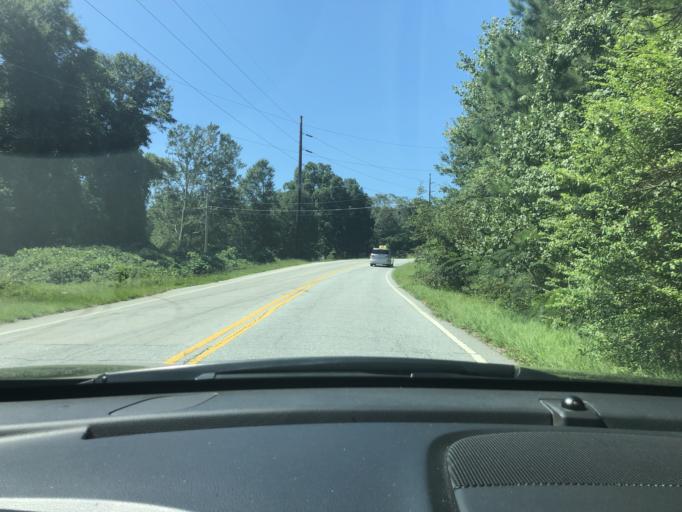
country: US
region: Georgia
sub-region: Gwinnett County
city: Grayson
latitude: 33.9274
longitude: -83.9529
